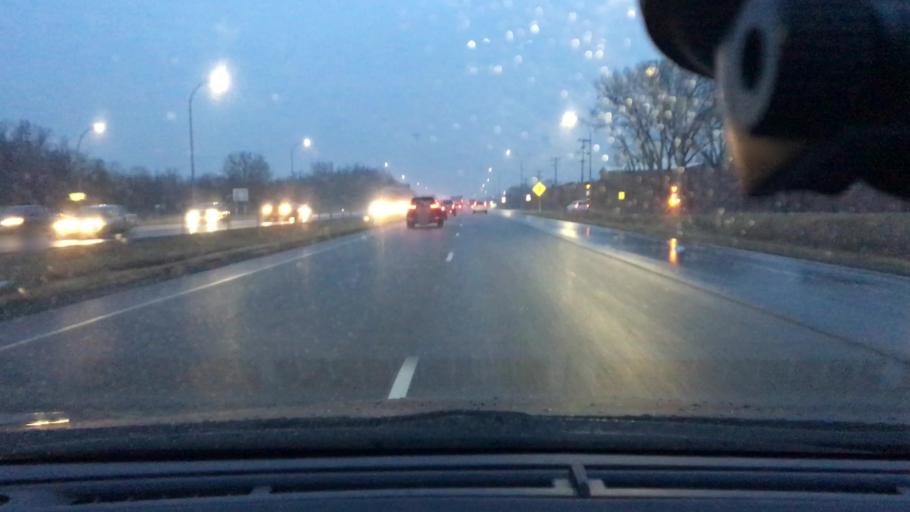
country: US
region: Minnesota
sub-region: Hennepin County
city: New Hope
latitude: 45.0352
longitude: -93.4006
